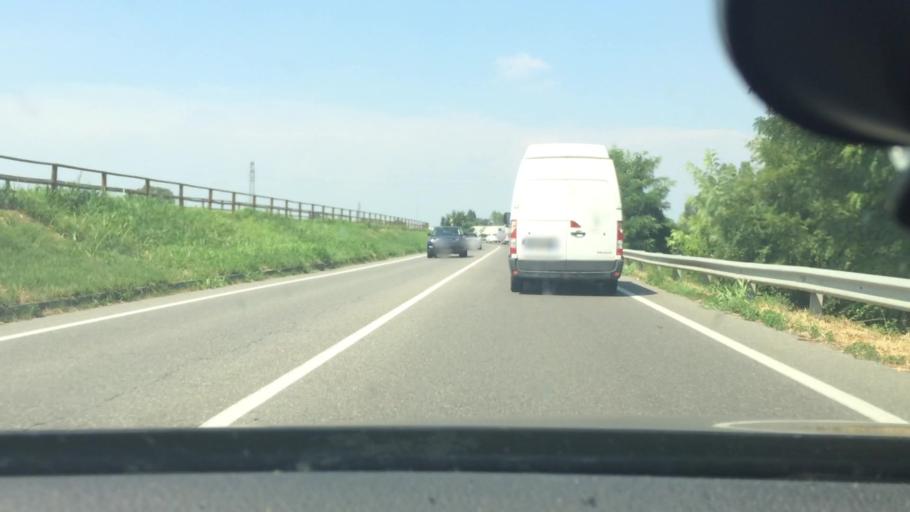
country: IT
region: Lombardy
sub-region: Provincia di Lodi
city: San Rocco al Porto
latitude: 45.0900
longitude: 9.6899
